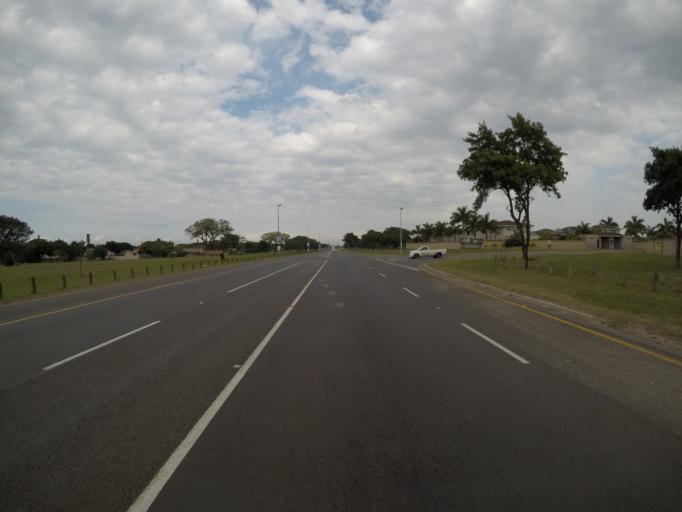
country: ZA
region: KwaZulu-Natal
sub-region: uThungulu District Municipality
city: Richards Bay
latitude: -28.7568
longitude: 32.0582
